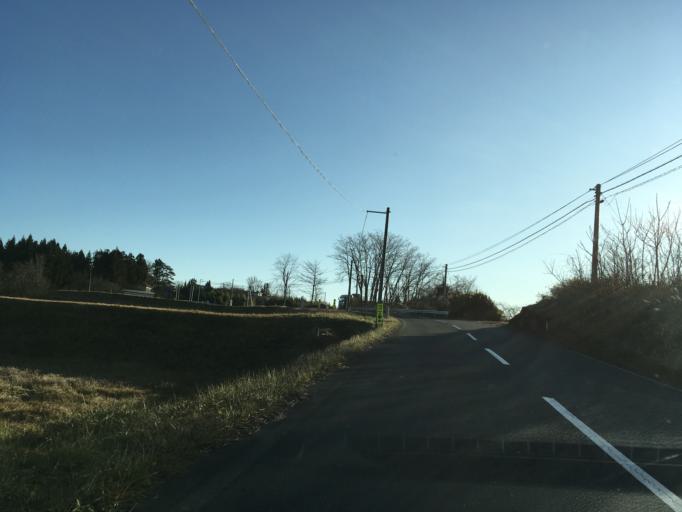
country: JP
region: Iwate
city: Ichinoseki
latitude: 38.7843
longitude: 141.2229
